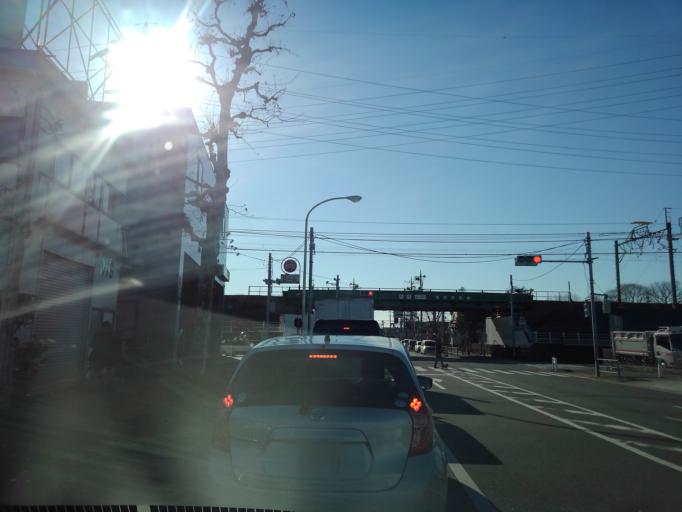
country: JP
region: Tokyo
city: Hino
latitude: 35.7284
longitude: 139.3825
